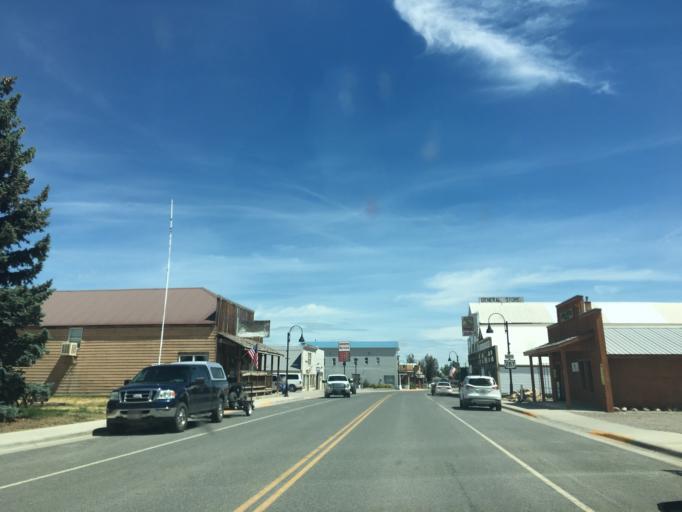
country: US
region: Montana
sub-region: Teton County
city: Choteau
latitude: 47.4928
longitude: -112.3917
